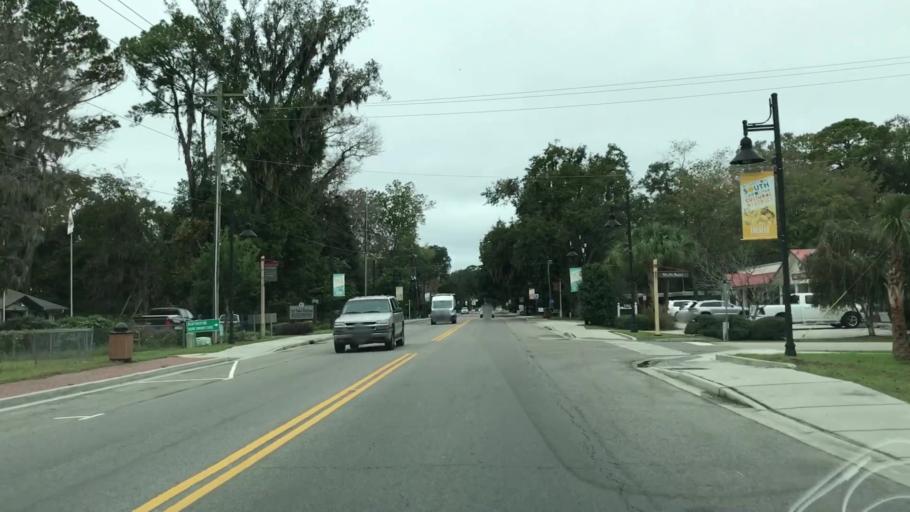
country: US
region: South Carolina
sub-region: Beaufort County
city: Bluffton
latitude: 32.2373
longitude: -80.8650
